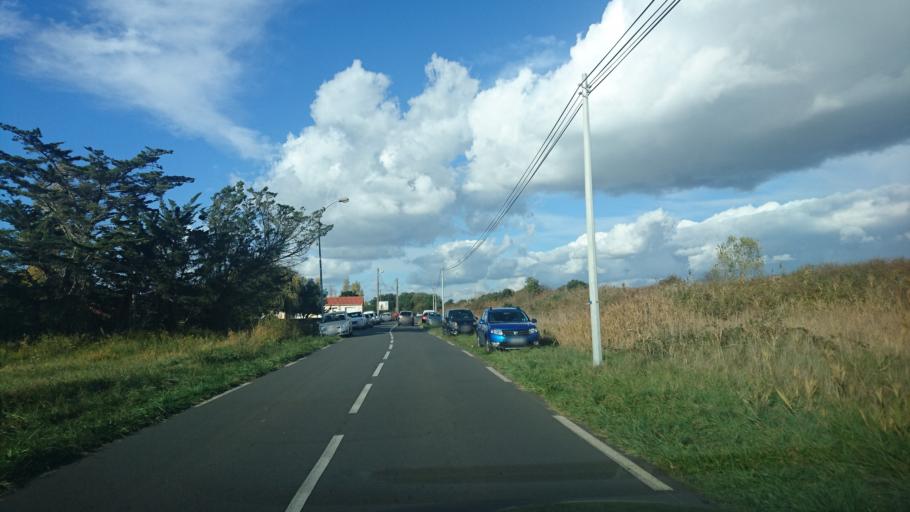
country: FR
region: Pays de la Loire
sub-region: Departement de la Vendee
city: Les Sables-d'Olonne
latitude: 46.5118
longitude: -1.8038
